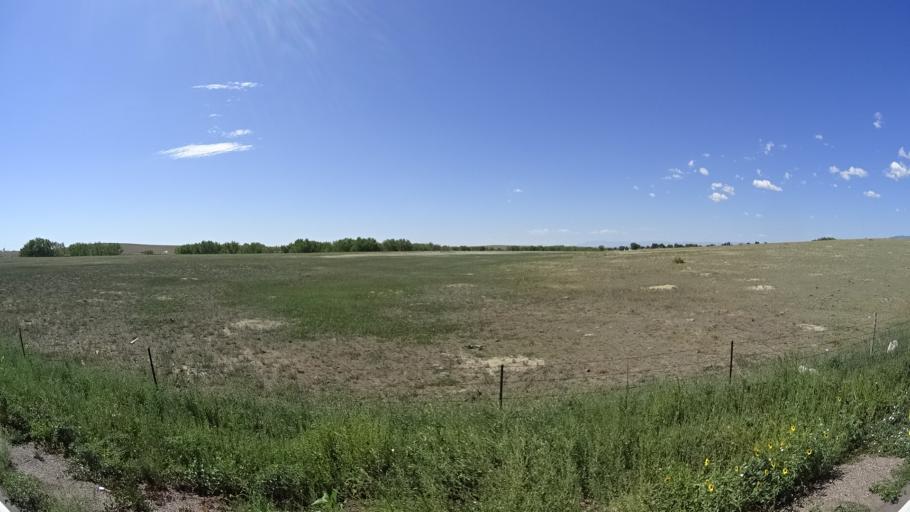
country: US
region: Colorado
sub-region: El Paso County
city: Security-Widefield
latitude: 38.7810
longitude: -104.6432
